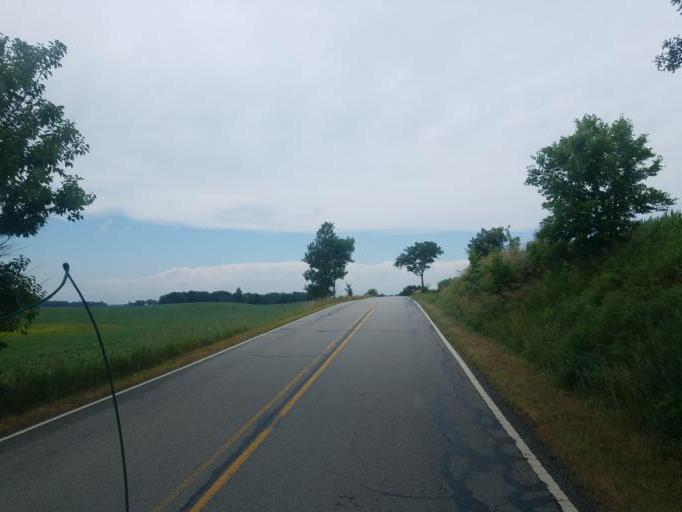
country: US
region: Indiana
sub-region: DeKalb County
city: Butler
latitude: 41.3866
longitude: -84.8177
